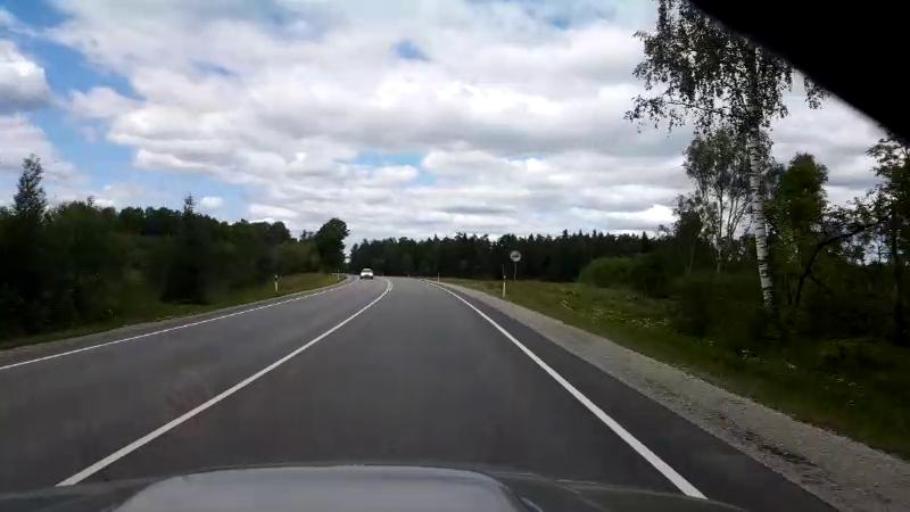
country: EE
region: Raplamaa
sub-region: Maerjamaa vald
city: Marjamaa
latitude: 58.9670
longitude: 24.4768
